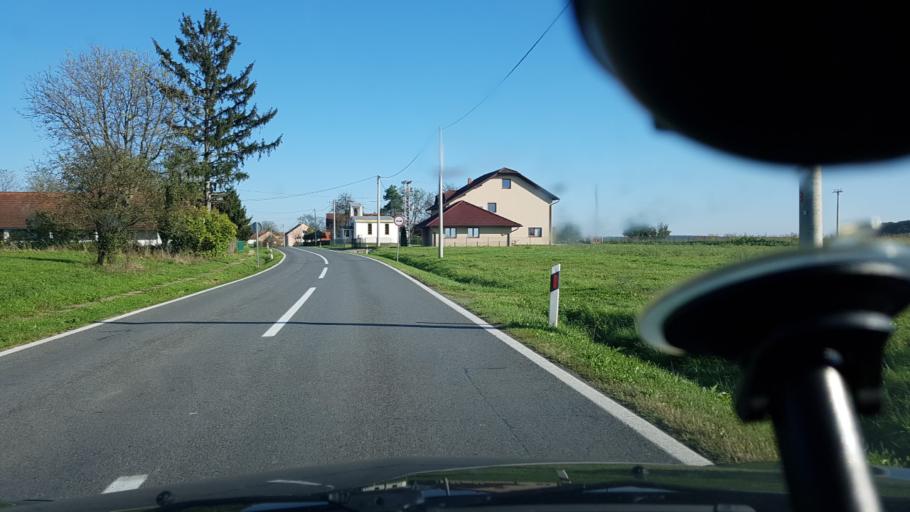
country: HR
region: Bjelovarsko-Bilogorska
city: Gudovac
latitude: 45.8332
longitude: 16.7886
